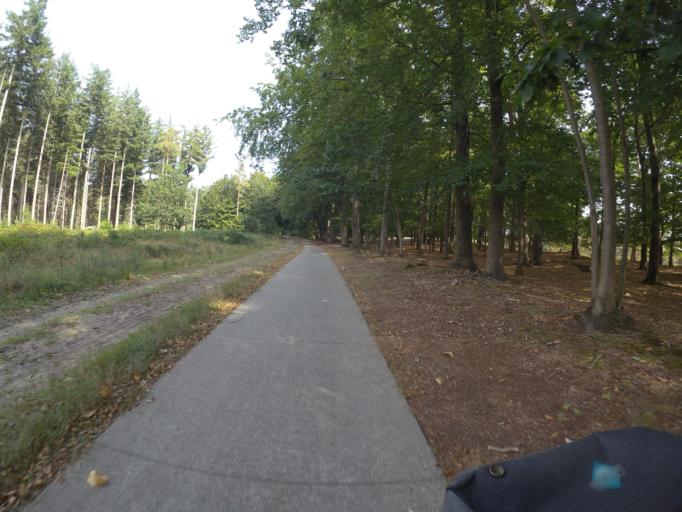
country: NL
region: Drenthe
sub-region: Gemeente Westerveld
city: Dwingeloo
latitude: 52.8878
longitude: 6.3238
